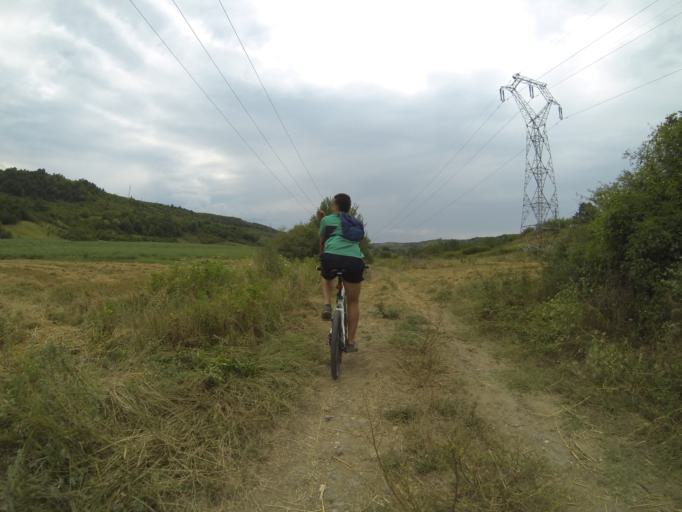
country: RO
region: Dolj
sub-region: Comuna Cotofenii din Fata
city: Cotofenii din Fata
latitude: 44.4843
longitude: 23.6801
